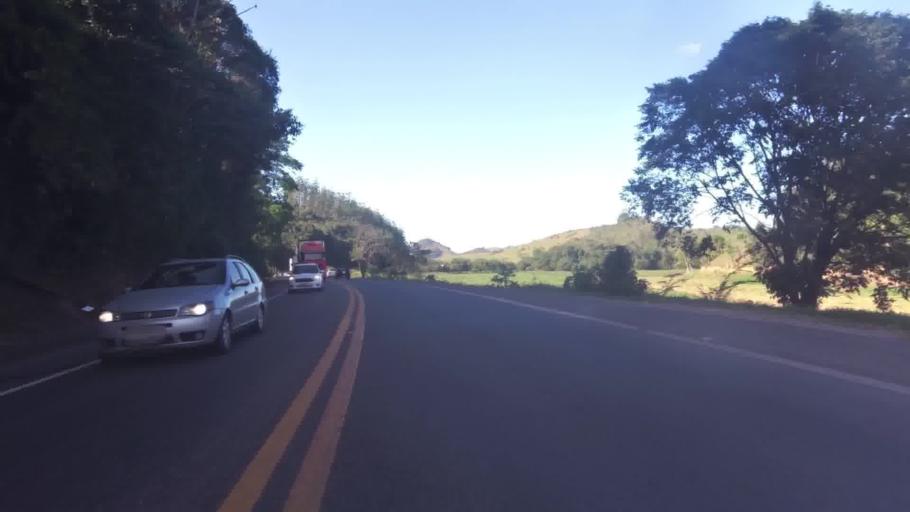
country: BR
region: Espirito Santo
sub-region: Iconha
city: Iconha
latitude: -20.8217
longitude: -40.8477
